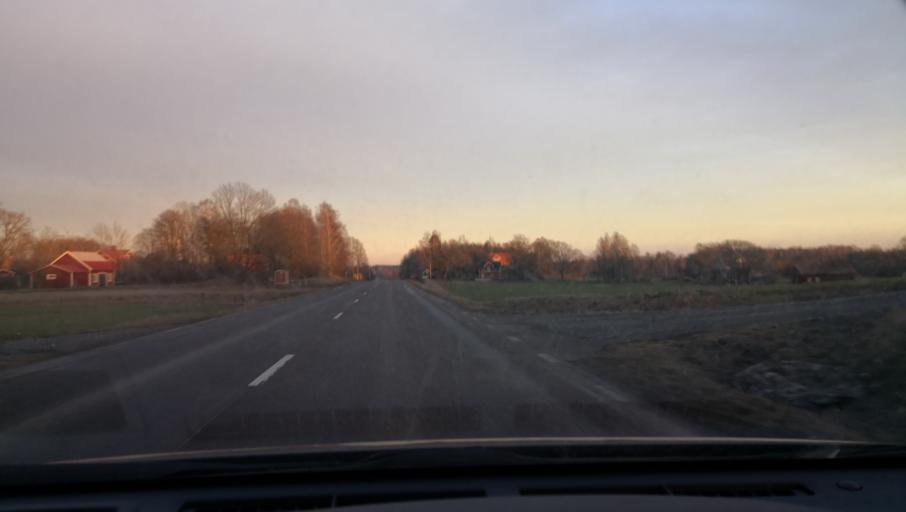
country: SE
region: OErebro
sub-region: Orebro Kommun
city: Vintrosa
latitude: 59.2432
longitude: 14.9906
